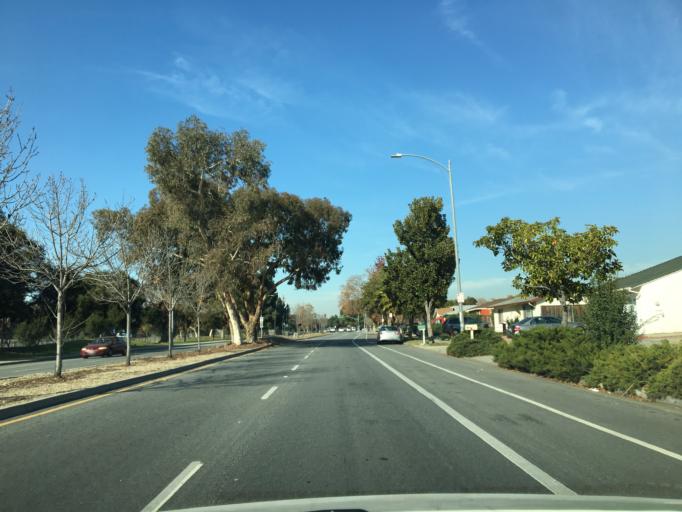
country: US
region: California
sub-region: Santa Clara County
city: Alum Rock
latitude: 37.3722
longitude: -121.8570
